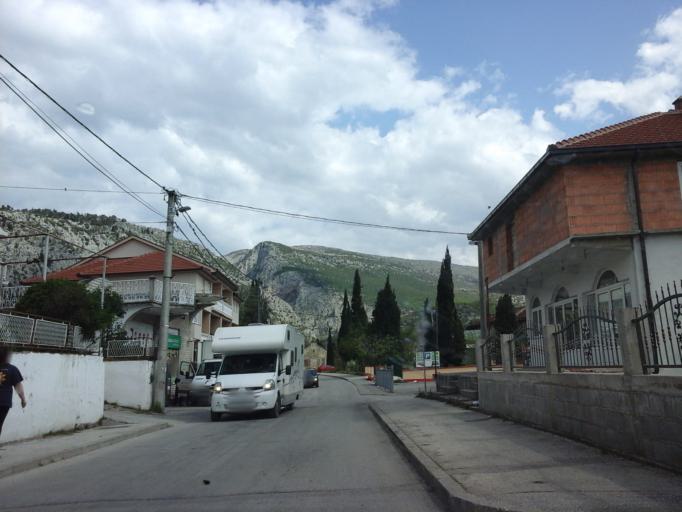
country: BA
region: Federation of Bosnia and Herzegovina
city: Blagaj
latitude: 43.2580
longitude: 17.8910
